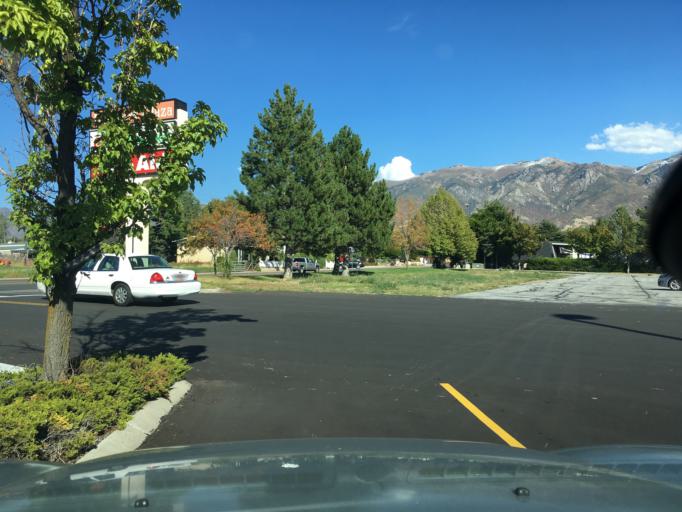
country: US
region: Utah
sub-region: Davis County
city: Layton
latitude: 41.0739
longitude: -111.9493
